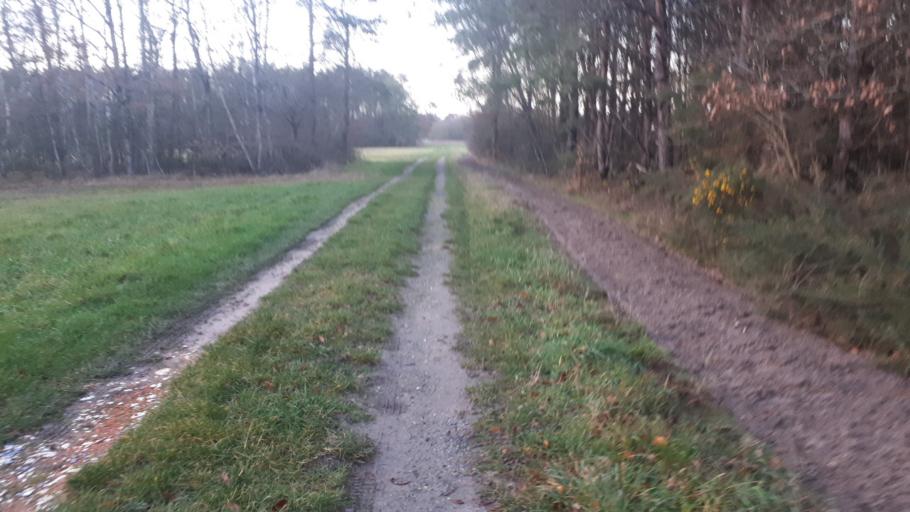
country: FR
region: Centre
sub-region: Departement du Loir-et-Cher
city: Saint-Romain-sur-Cher
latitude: 47.3482
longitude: 1.3996
